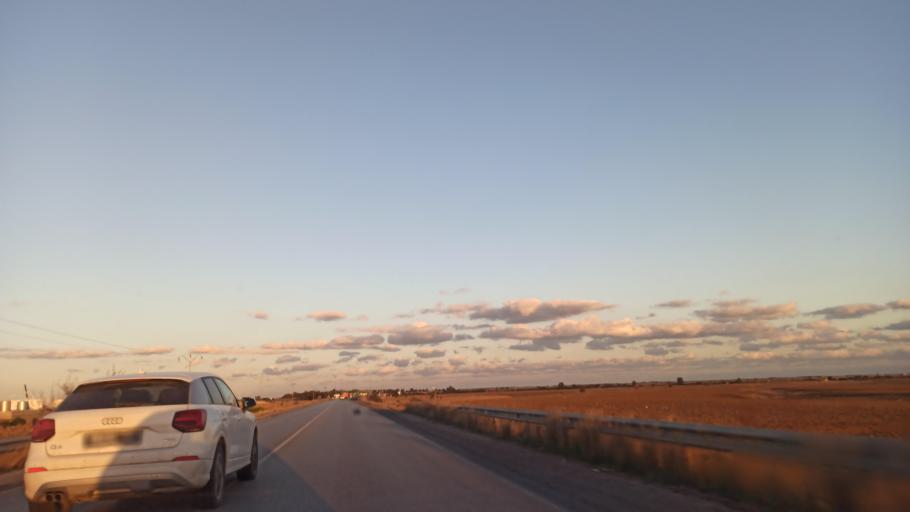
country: TN
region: Susah
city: Harqalah
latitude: 36.1032
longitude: 10.3929
